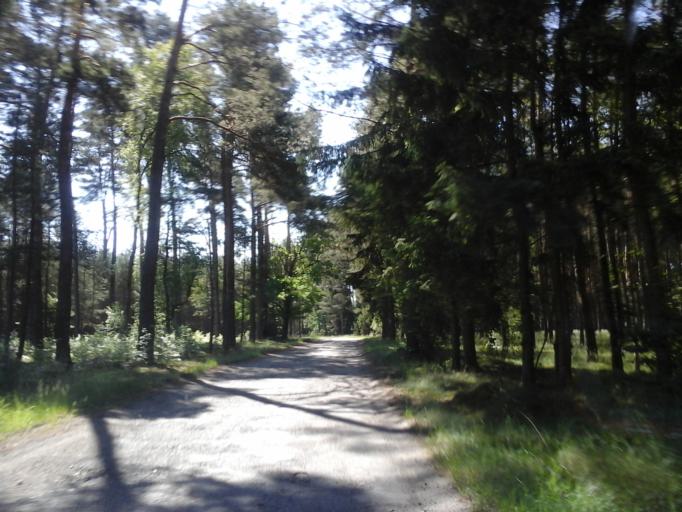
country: PL
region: West Pomeranian Voivodeship
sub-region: Powiat choszczenski
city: Drawno
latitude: 53.1362
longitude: 15.8895
